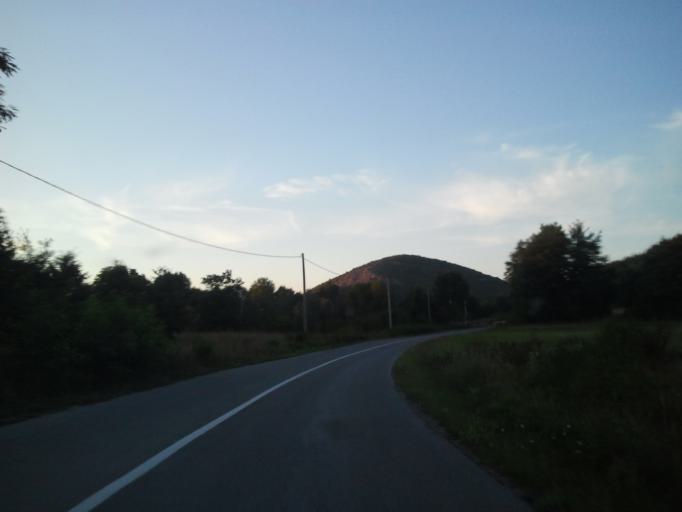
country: HR
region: Zadarska
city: Obrovac
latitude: 44.4203
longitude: 15.6601
